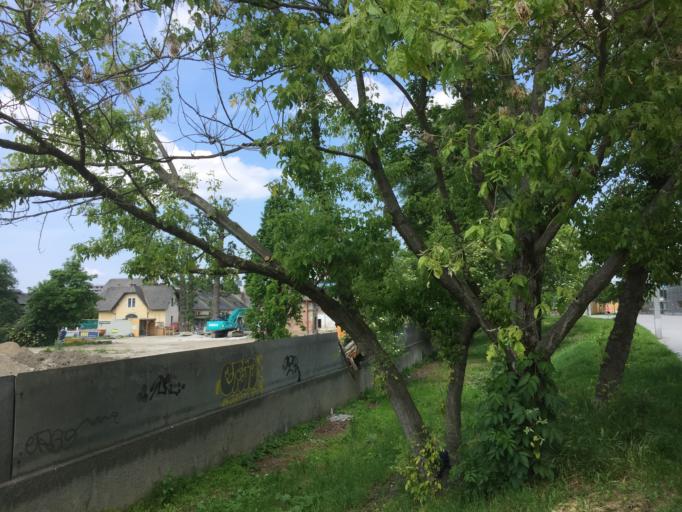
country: AT
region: Vienna
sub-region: Wien Stadt
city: Vienna
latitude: 48.2103
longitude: 16.4201
